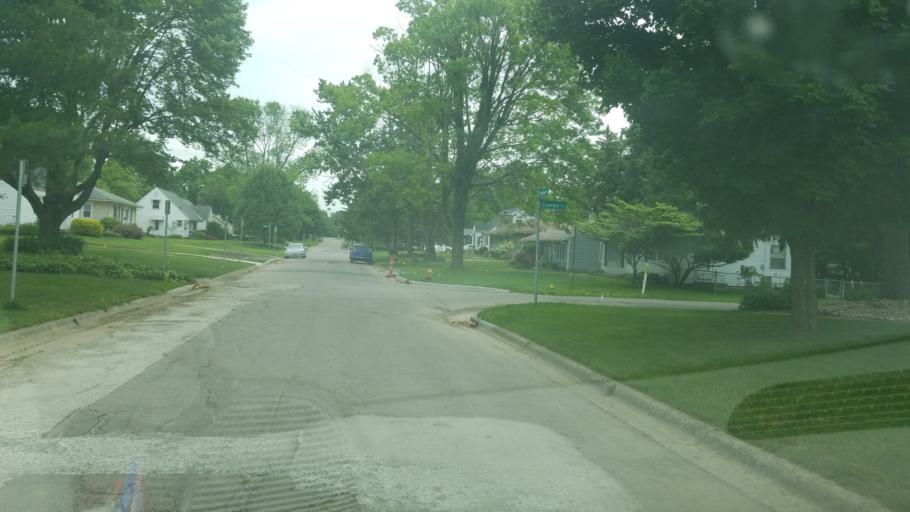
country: US
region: Ohio
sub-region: Franklin County
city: Worthington
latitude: 40.0581
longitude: -83.0044
